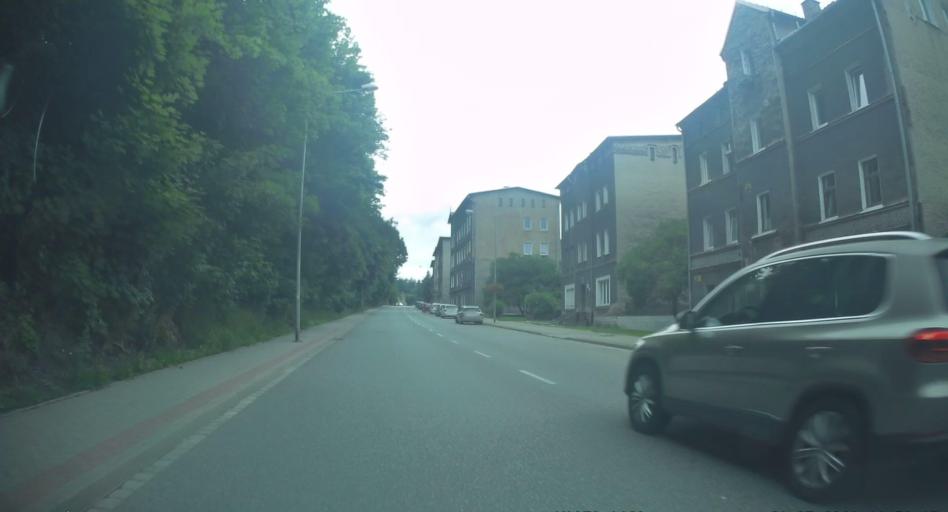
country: PL
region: Lower Silesian Voivodeship
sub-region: Powiat walbrzyski
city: Walbrzych
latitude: 50.7696
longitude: 16.3088
